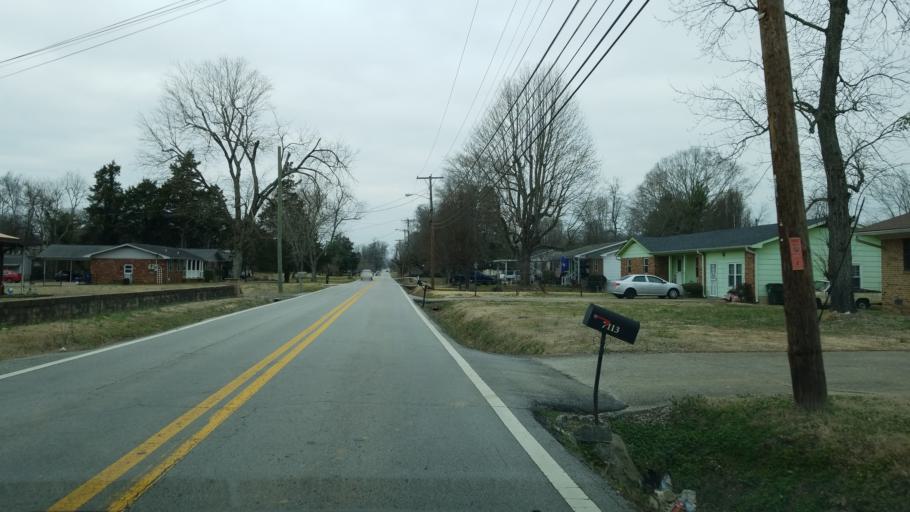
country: US
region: Tennessee
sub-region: Hamilton County
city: East Brainerd
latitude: 35.0534
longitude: -85.1529
